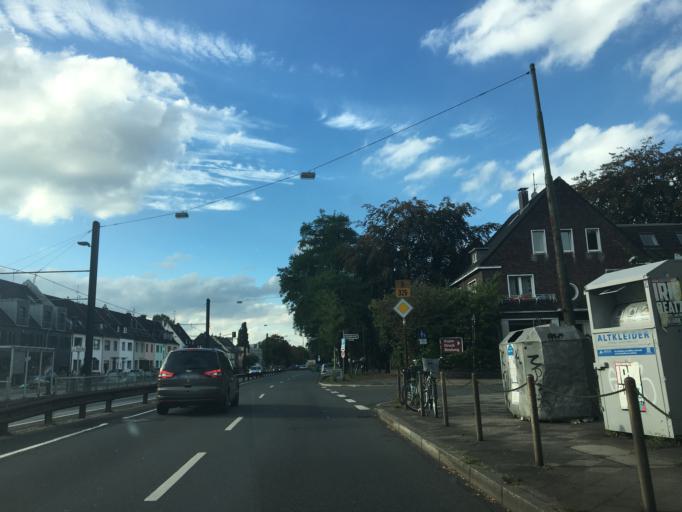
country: DE
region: North Rhine-Westphalia
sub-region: Regierungsbezirk Dusseldorf
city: Dusseldorf
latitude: 51.2001
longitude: 6.7898
